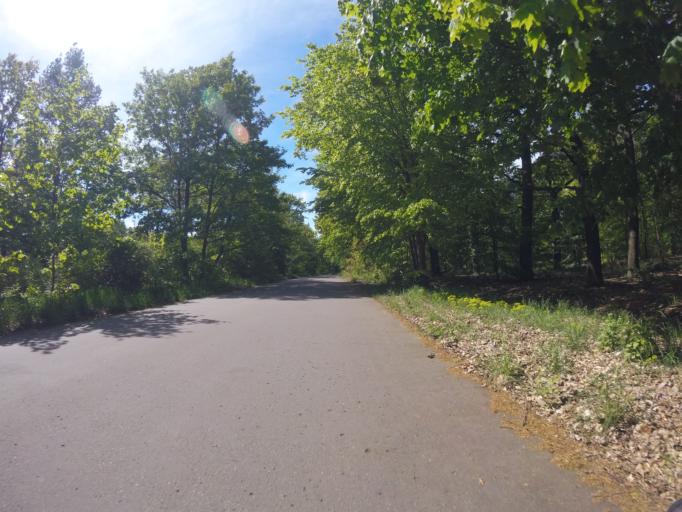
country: DE
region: Berlin
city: Nikolassee
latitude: 52.4510
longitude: 13.2128
